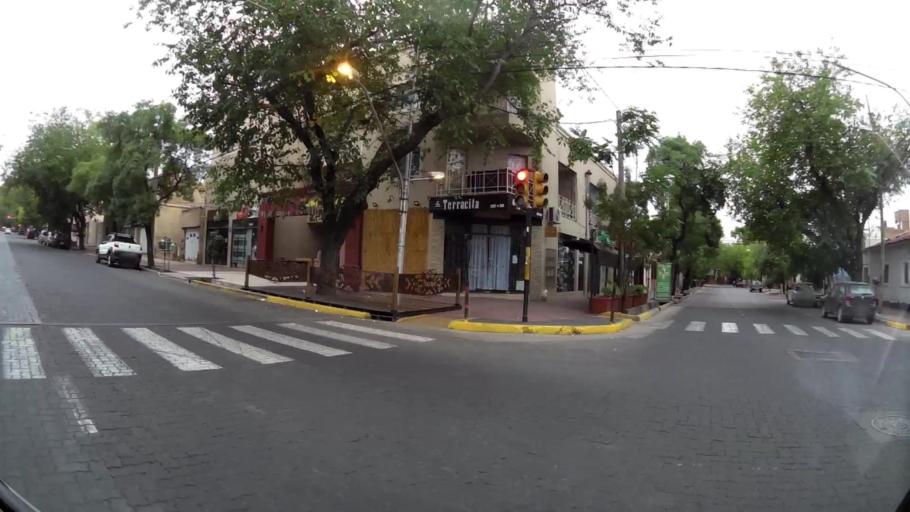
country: AR
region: Mendoza
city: Mendoza
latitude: -32.8835
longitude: -68.8587
